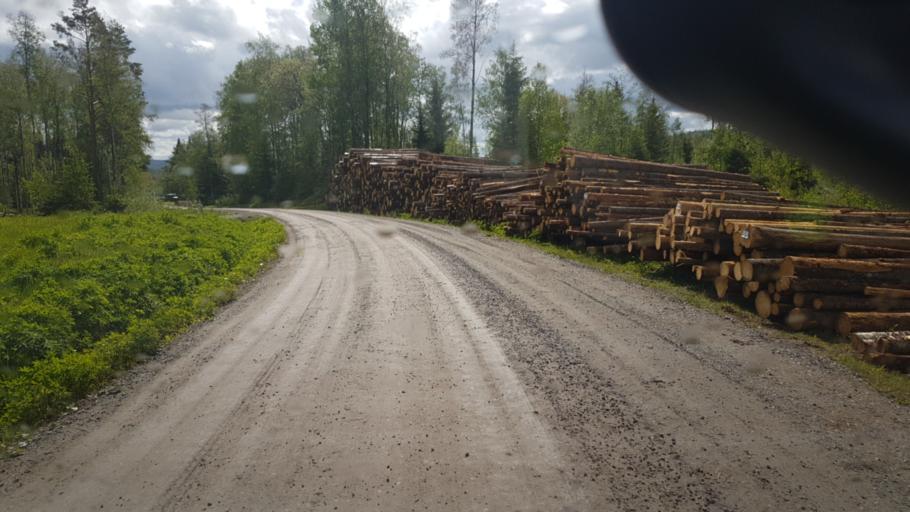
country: NO
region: Ostfold
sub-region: Romskog
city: Romskog
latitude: 59.7030
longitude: 12.0541
